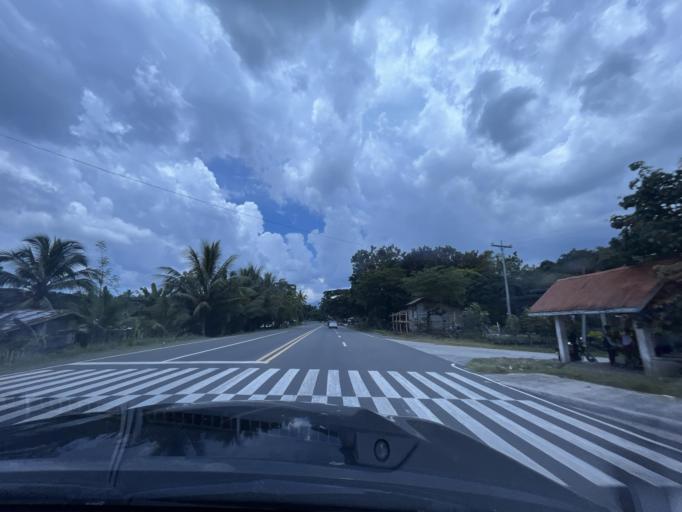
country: PH
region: Soccsksargen
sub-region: Province of Sarangani
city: Malandag
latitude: 6.4316
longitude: 125.3045
